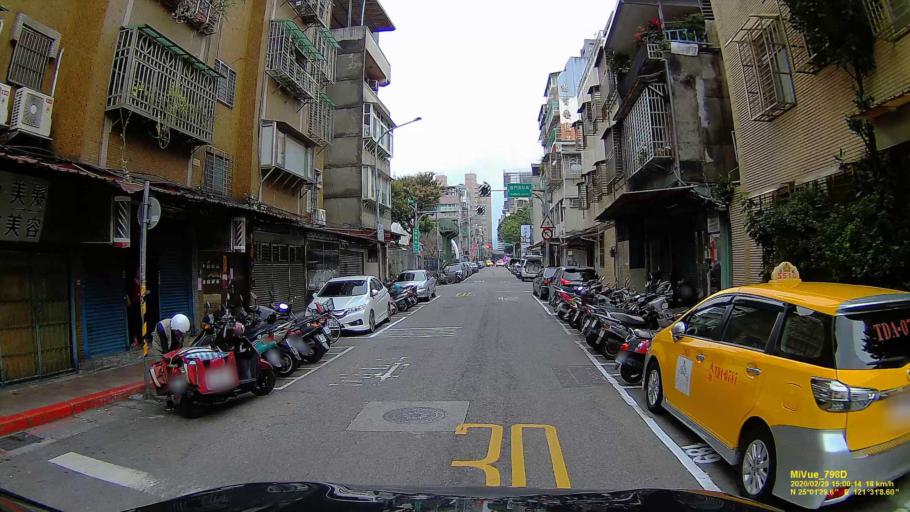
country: TW
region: Taipei
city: Taipei
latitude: 25.0248
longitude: 121.5191
